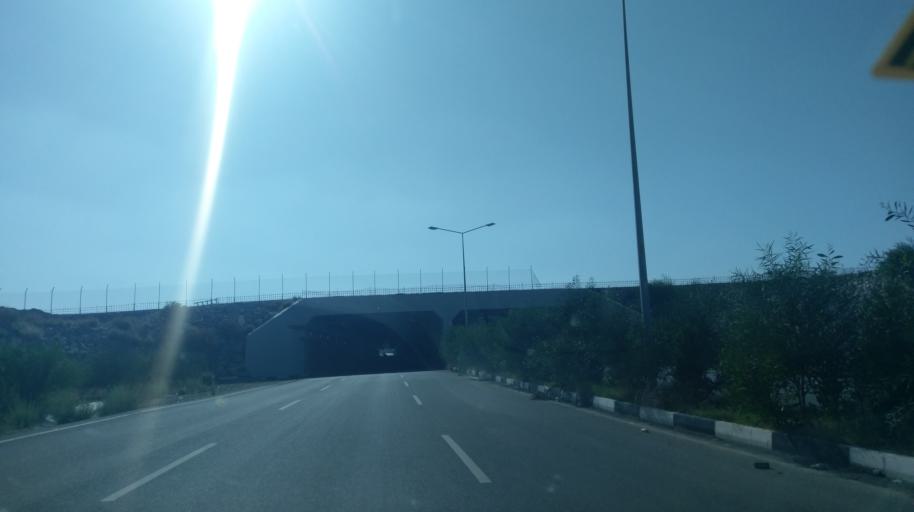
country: CY
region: Larnaka
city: Athienou
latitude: 35.1519
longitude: 33.5194
